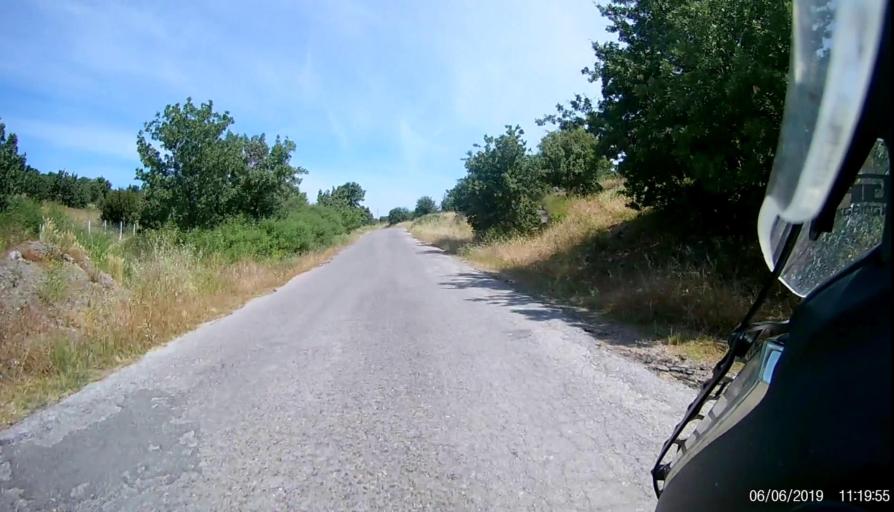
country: TR
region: Canakkale
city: Gulpinar
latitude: 39.6613
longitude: 26.1640
